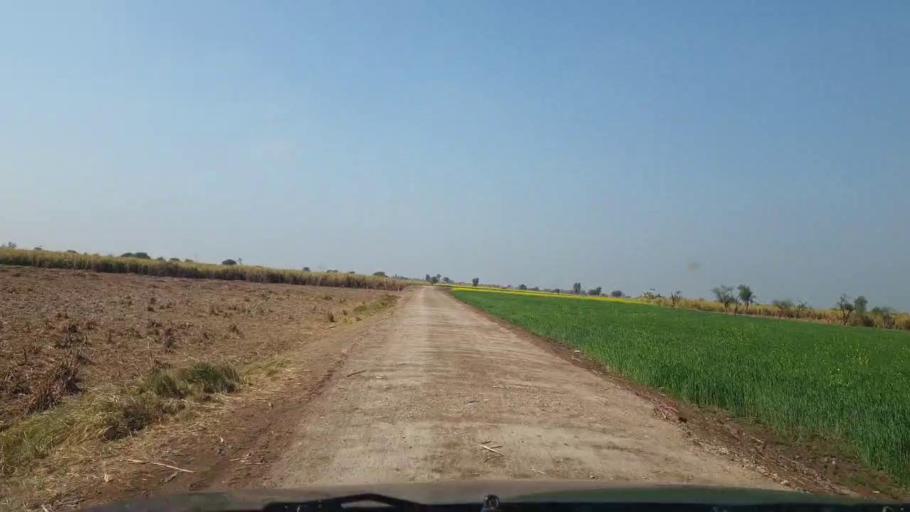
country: PK
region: Sindh
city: Sinjhoro
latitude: 26.0457
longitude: 68.7424
